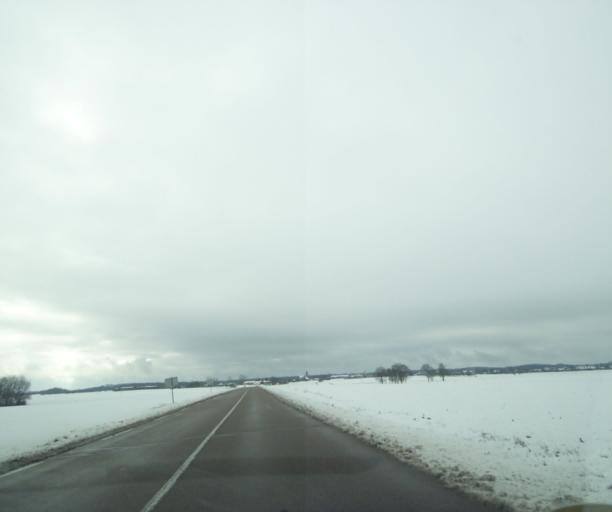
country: FR
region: Champagne-Ardenne
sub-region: Departement de la Haute-Marne
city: Montier-en-Der
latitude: 48.4422
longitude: 4.7320
